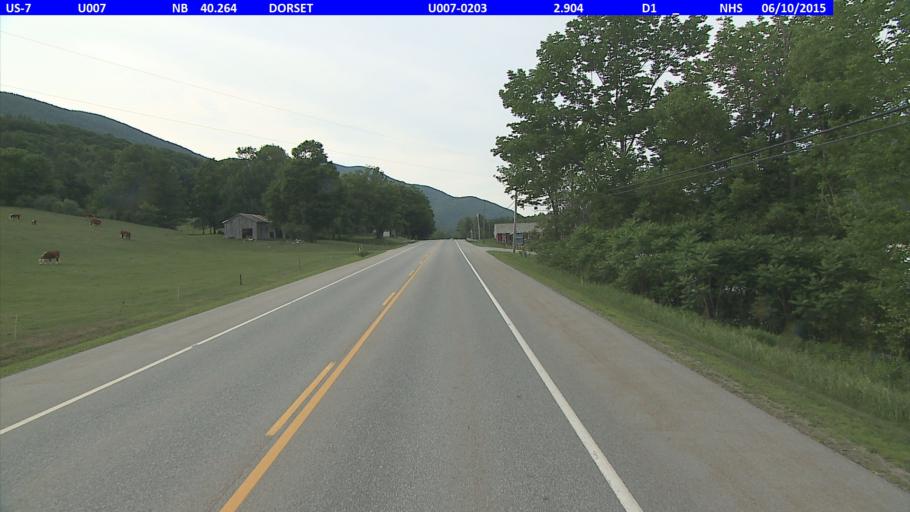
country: US
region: Vermont
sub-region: Bennington County
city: Manchester Center
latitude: 43.2513
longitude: -73.0079
